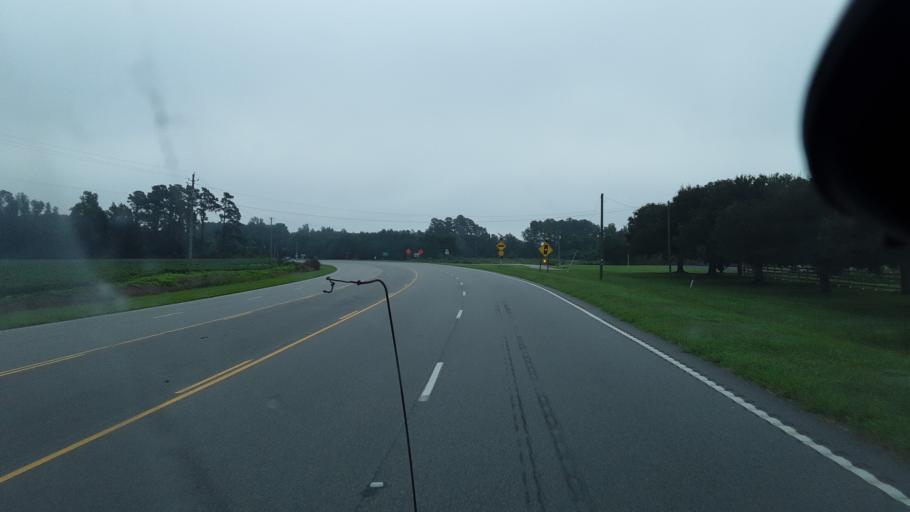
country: US
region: South Carolina
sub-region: Florence County
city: Johnsonville
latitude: 33.8818
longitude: -79.4576
